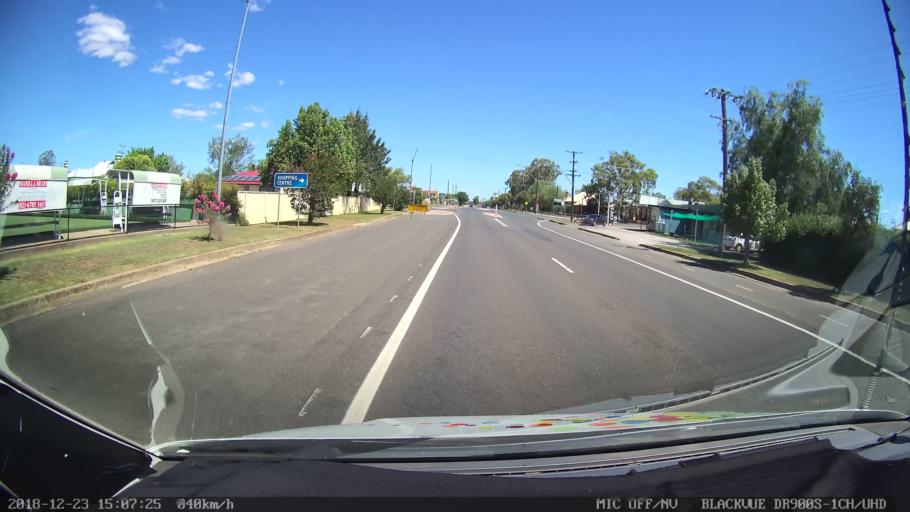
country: AU
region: New South Wales
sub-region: Tamworth Municipality
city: Manilla
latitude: -30.7478
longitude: 150.7244
